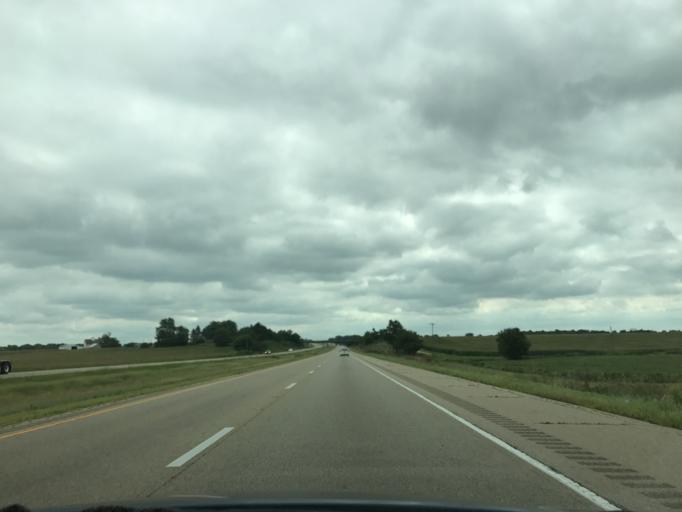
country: US
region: Illinois
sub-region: Bureau County
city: Ladd
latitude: 41.3807
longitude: -89.2649
